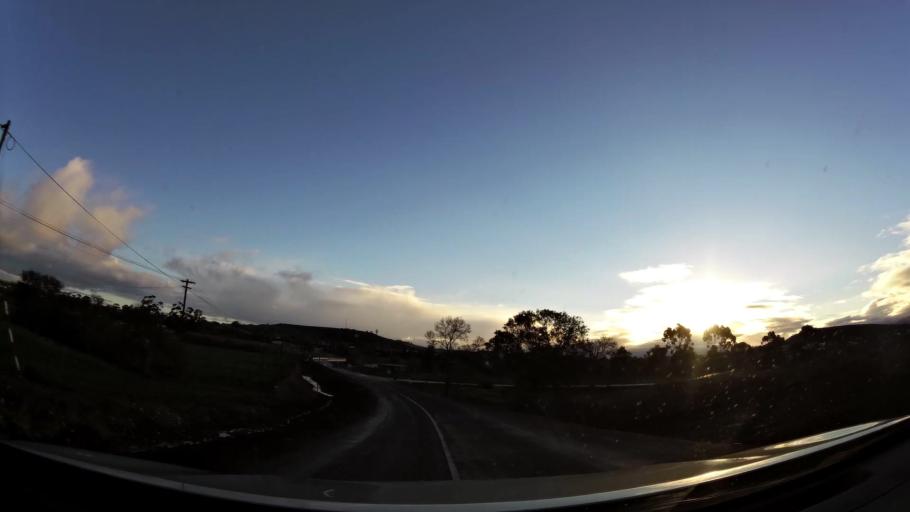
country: ZA
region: Western Cape
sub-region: Eden District Municipality
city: Riversdale
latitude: -34.0921
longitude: 20.9678
